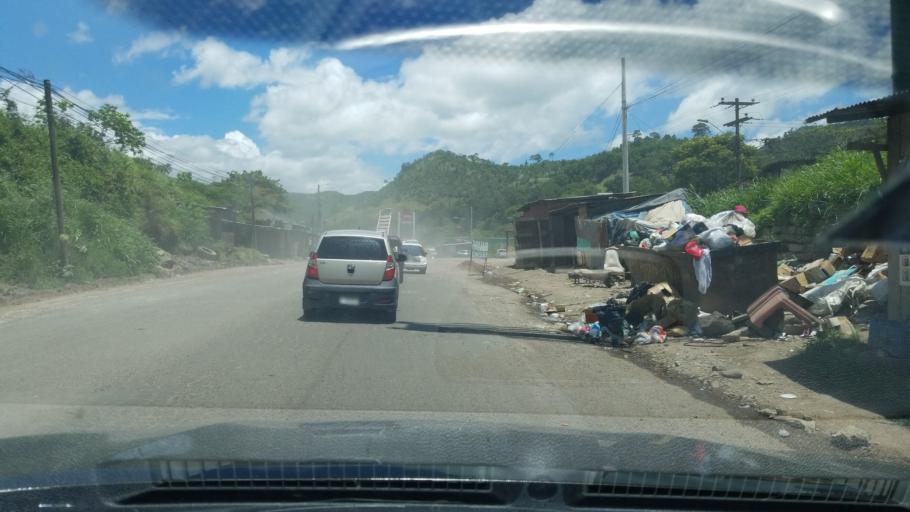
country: HN
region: Francisco Morazan
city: Rio Abajo
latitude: 14.1386
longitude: -87.2321
